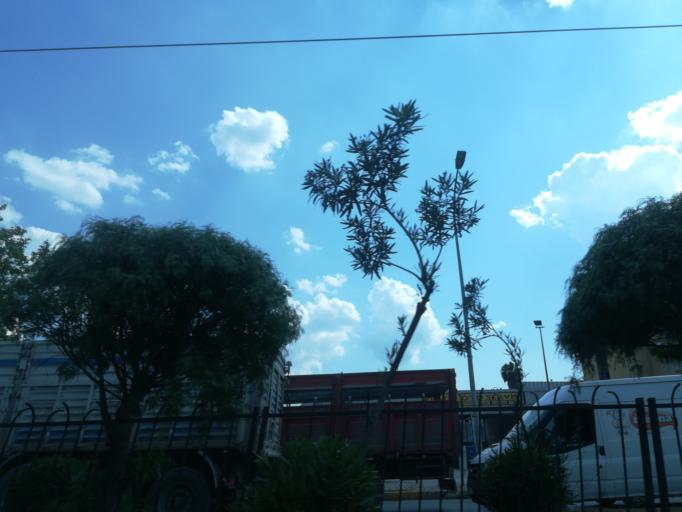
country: TR
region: Adana
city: Yuregir
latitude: 36.9880
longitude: 35.3486
